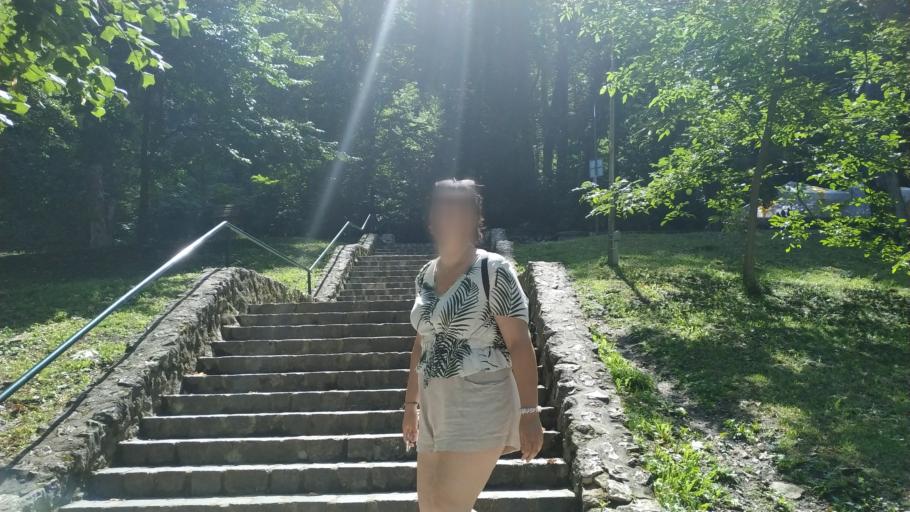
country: RO
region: Brasov
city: Brasov
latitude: 45.6397
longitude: 25.5938
